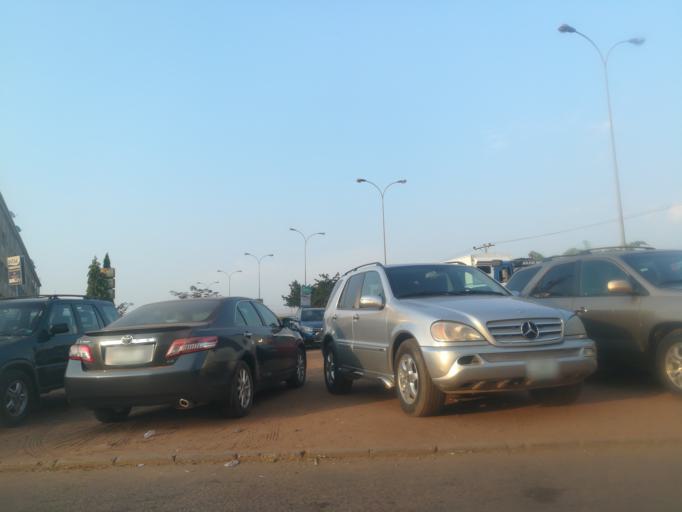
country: NG
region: Abuja Federal Capital Territory
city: Abuja
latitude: 9.0664
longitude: 7.4465
